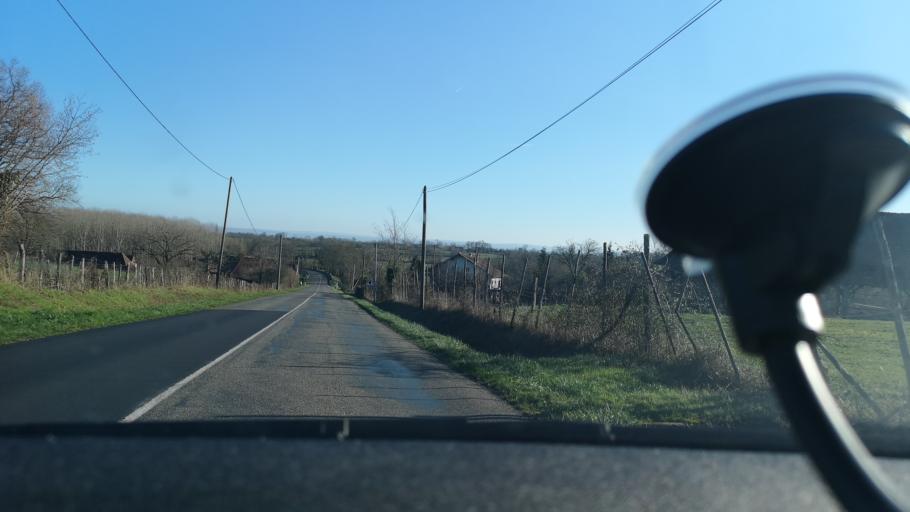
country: FR
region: Bourgogne
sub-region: Departement de Saone-et-Loire
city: Saint-Germain-du-Bois
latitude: 46.7503
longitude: 5.2874
